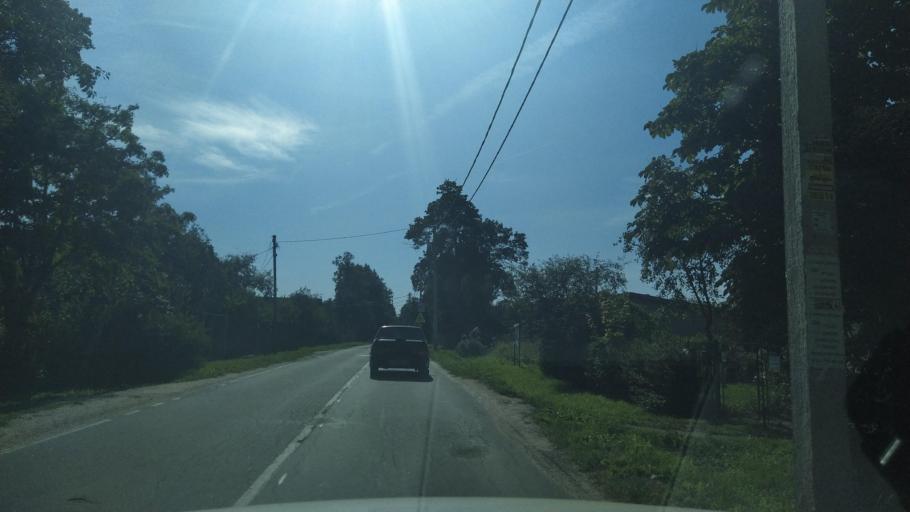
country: RU
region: Leningrad
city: Siverskiy
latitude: 59.3298
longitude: 30.0362
